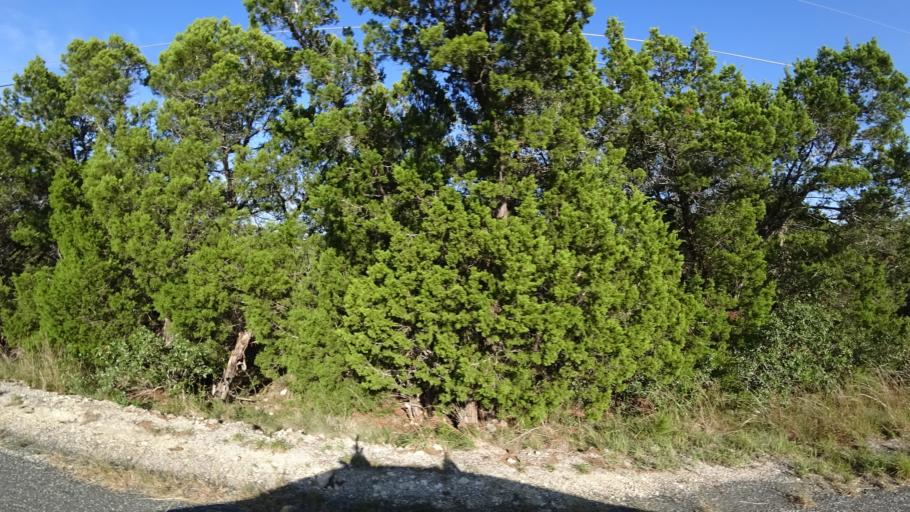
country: US
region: Texas
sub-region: Travis County
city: Bee Cave
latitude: 30.2341
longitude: -97.9289
